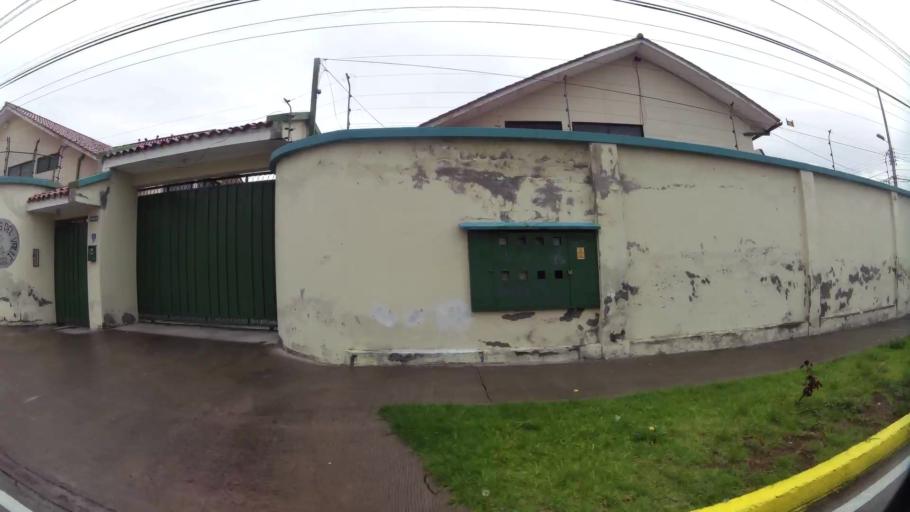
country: EC
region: Pichincha
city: Sangolqui
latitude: -0.2919
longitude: -78.4571
